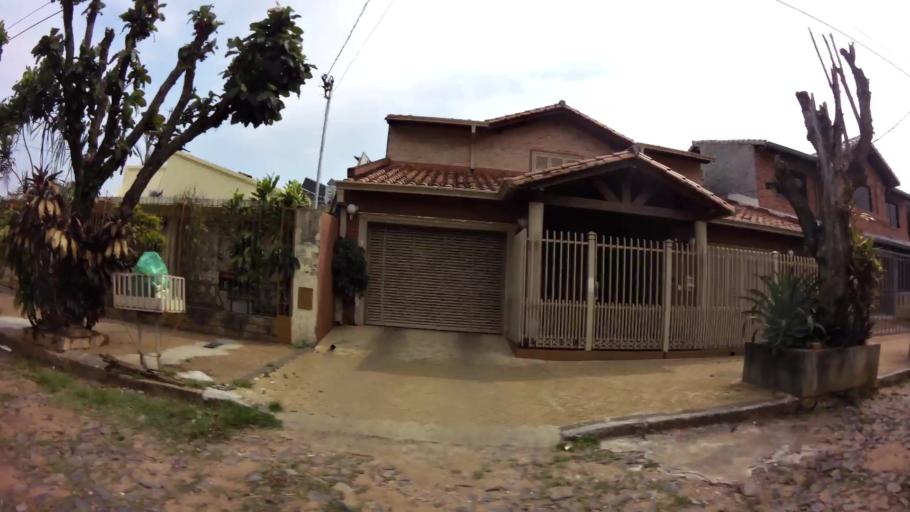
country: PY
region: Central
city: Fernando de la Mora
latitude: -25.2765
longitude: -57.5574
